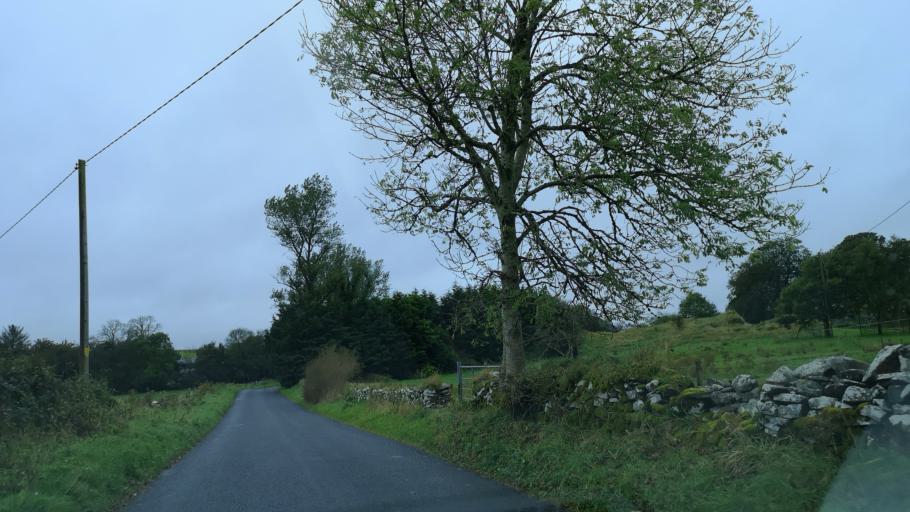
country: IE
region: Connaught
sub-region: Roscommon
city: Ballaghaderreen
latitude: 53.8971
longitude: -8.5997
